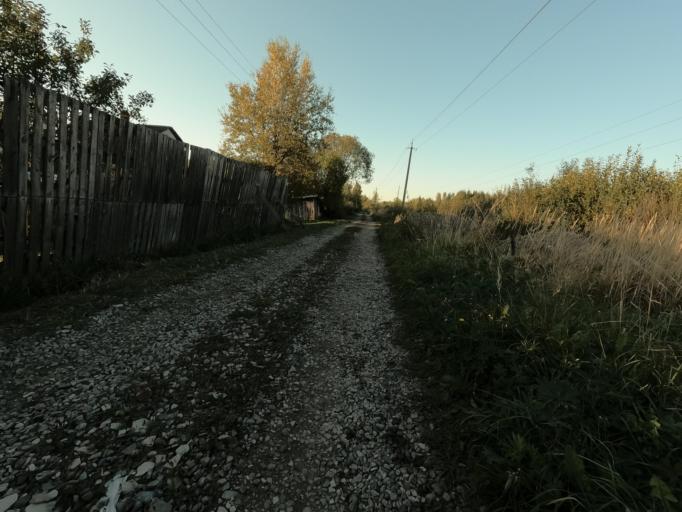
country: RU
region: Leningrad
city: Nikol'skoye
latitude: 59.7094
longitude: 30.7979
